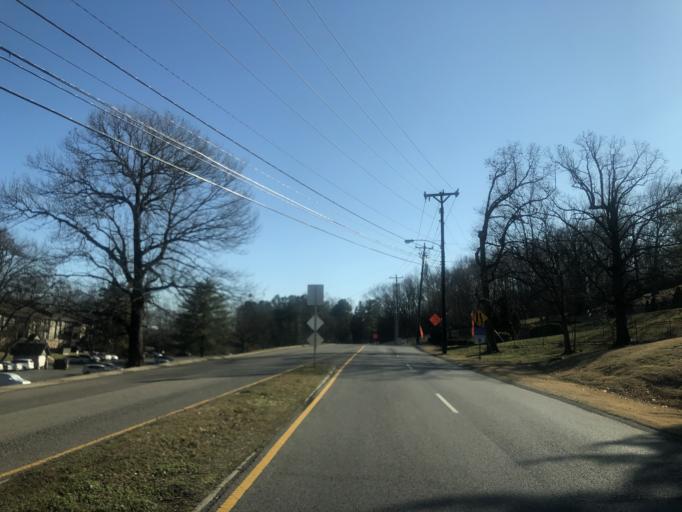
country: US
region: Tennessee
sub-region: Rutherford County
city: La Vergne
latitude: 36.0408
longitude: -86.6605
